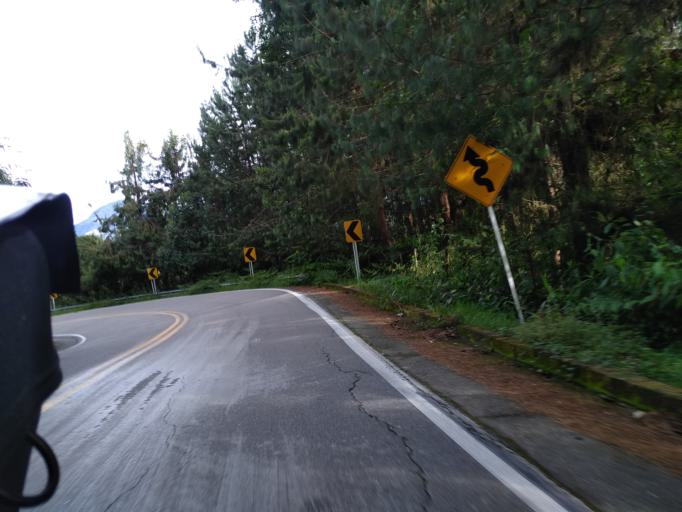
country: CO
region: Tolima
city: Herveo
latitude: 5.1381
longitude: -75.1748
